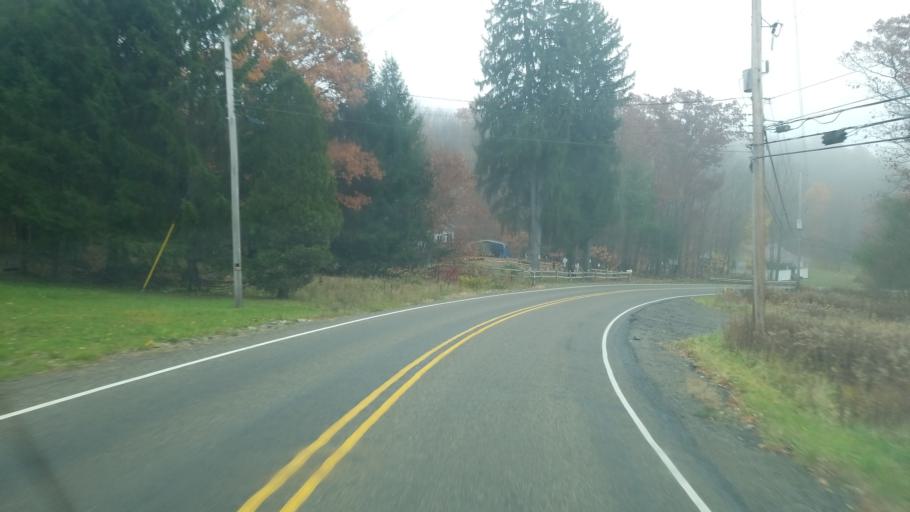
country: US
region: Pennsylvania
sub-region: McKean County
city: Foster Brook
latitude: 41.9066
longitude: -78.5282
